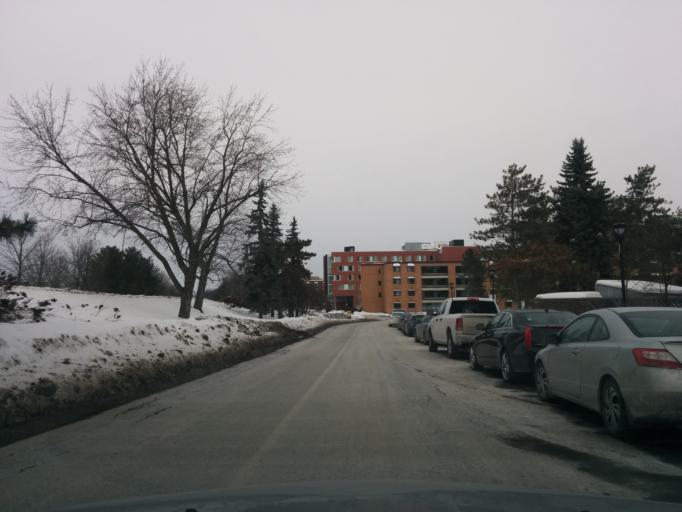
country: CA
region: Ontario
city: Ottawa
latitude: 45.3844
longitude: -75.6989
